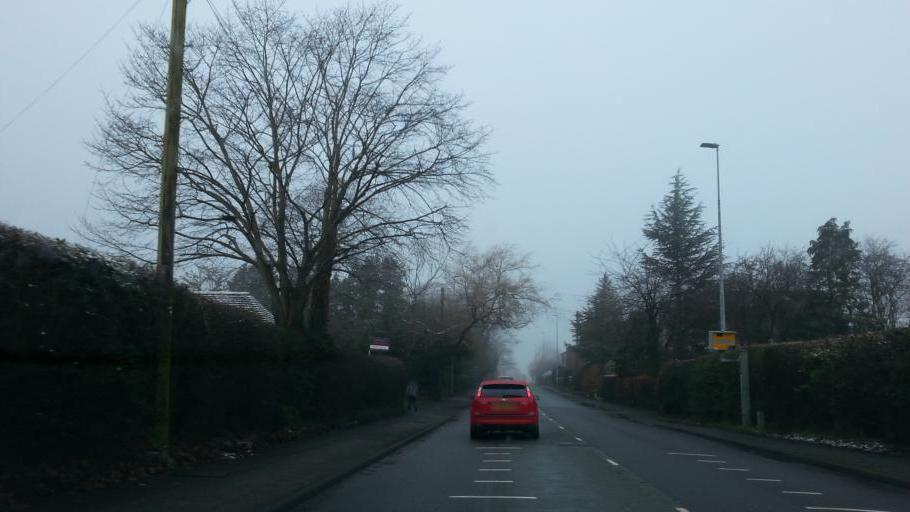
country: GB
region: England
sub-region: Cheshire East
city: Congleton
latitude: 53.1553
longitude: -2.1878
